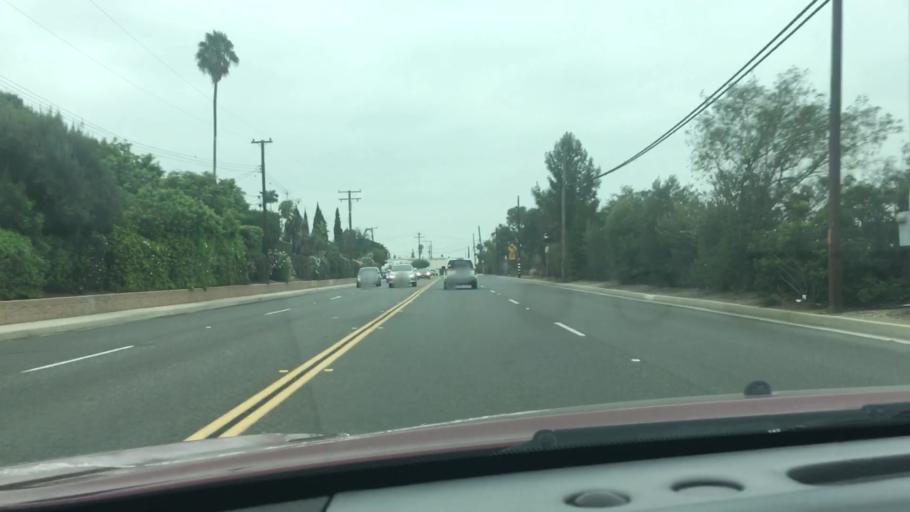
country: US
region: California
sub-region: Orange County
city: Buena Park
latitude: 33.8843
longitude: -118.0052
